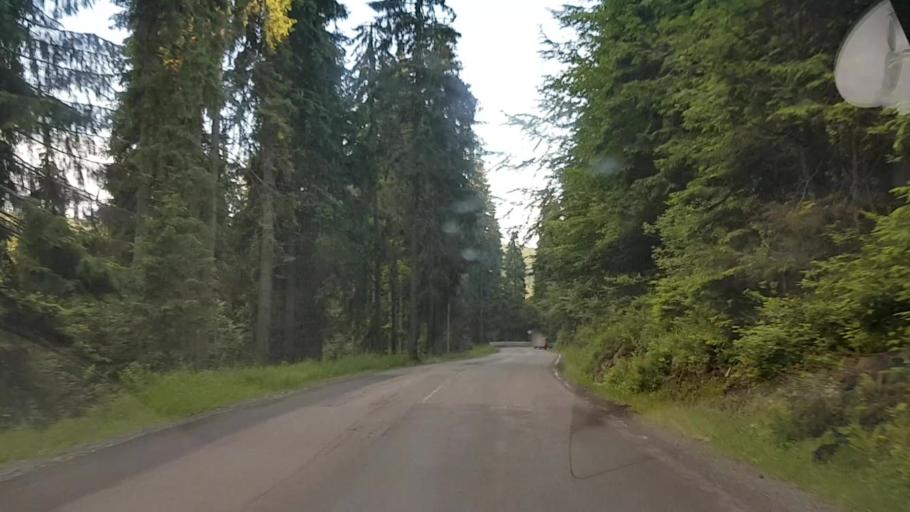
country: RO
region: Harghita
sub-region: Comuna Varsag
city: Varsag
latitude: 46.6479
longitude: 25.2882
